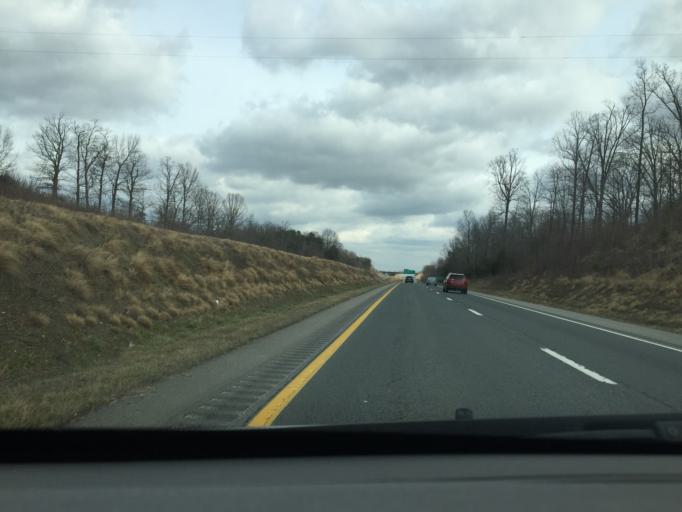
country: US
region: Virginia
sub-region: Campbell County
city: Timberlake
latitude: 37.3245
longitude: -79.2149
